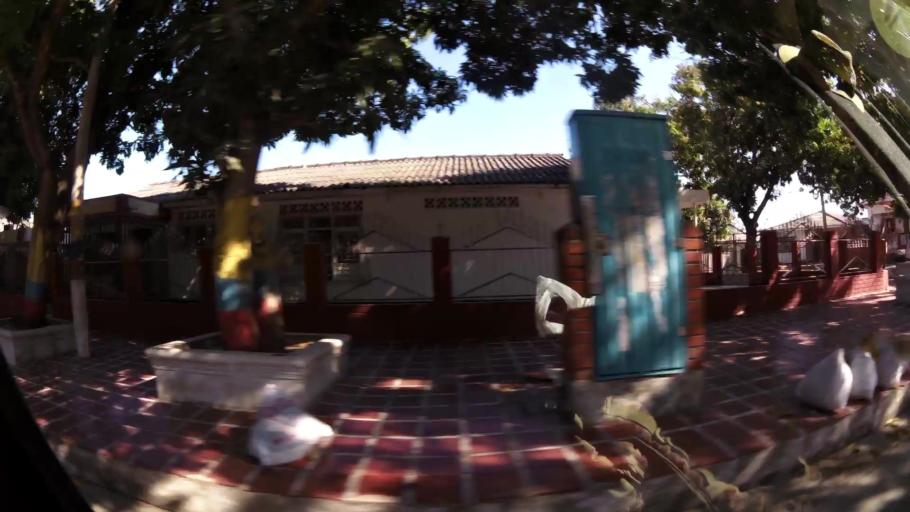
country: CO
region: Atlantico
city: Barranquilla
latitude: 10.9563
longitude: -74.7895
